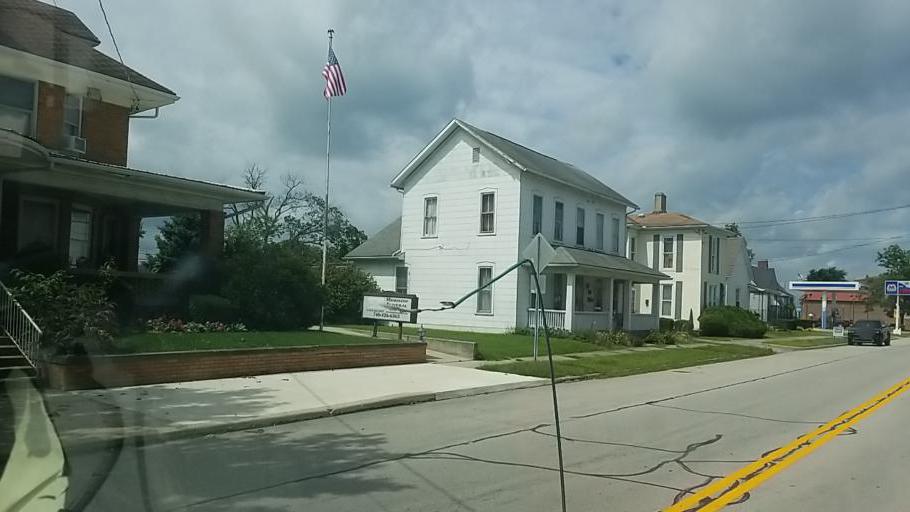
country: US
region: Ohio
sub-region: Fayette County
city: Jeffersonville
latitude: 39.6522
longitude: -83.5612
